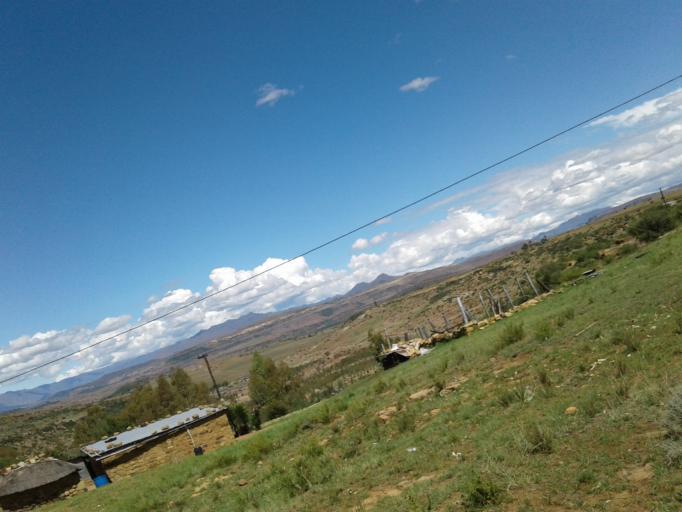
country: LS
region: Quthing
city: Quthing
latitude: -30.3638
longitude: 27.5482
